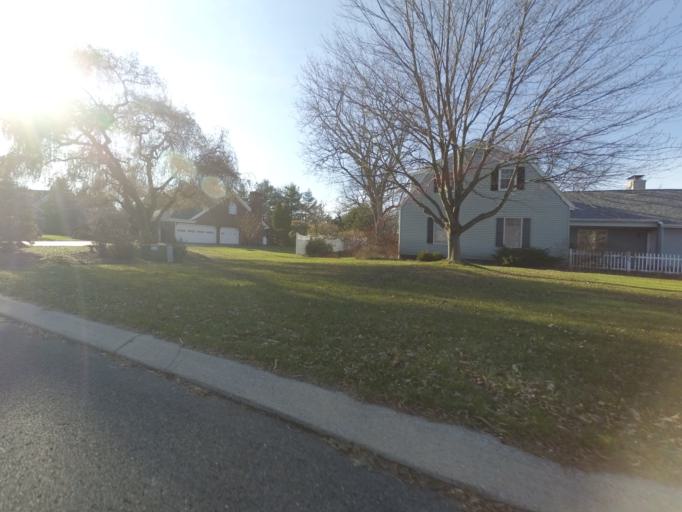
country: US
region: Pennsylvania
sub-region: Centre County
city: Lemont
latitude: 40.7945
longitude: -77.8274
